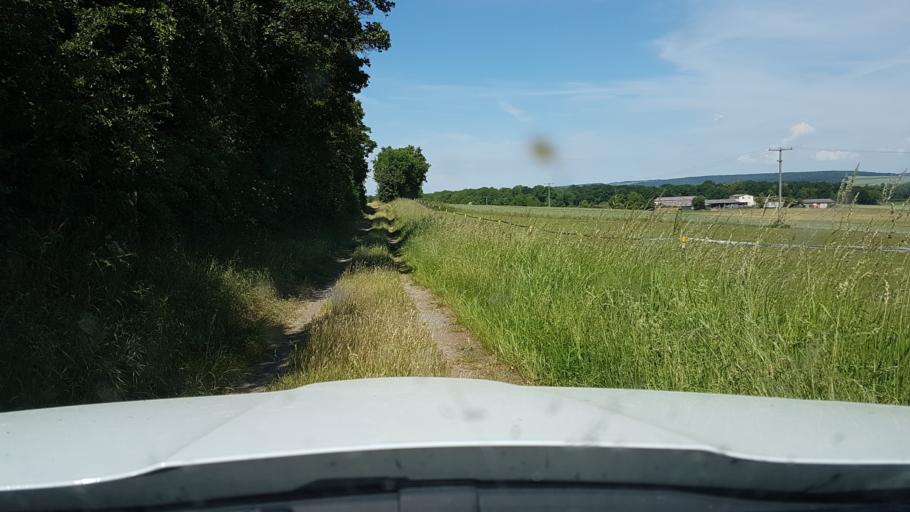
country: DE
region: Bavaria
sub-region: Regierungsbezirk Unterfranken
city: Wonfurt
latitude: 49.9963
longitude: 10.4940
